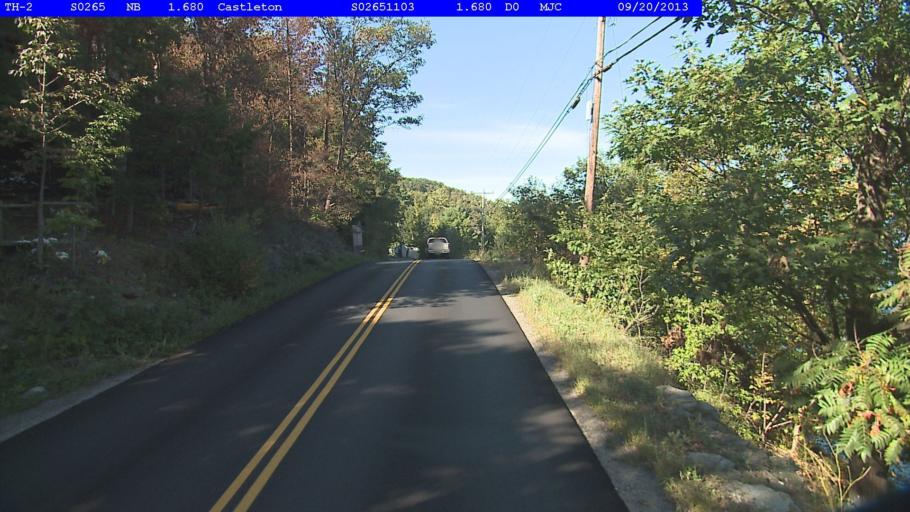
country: US
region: Vermont
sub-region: Rutland County
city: Fair Haven
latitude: 43.6268
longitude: -73.2329
